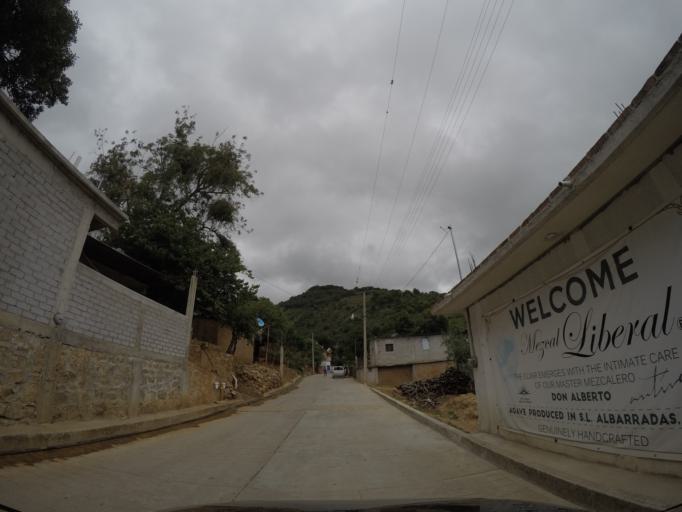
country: MX
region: Oaxaca
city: San Lorenzo Albarradas
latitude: 16.9027
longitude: -96.2616
